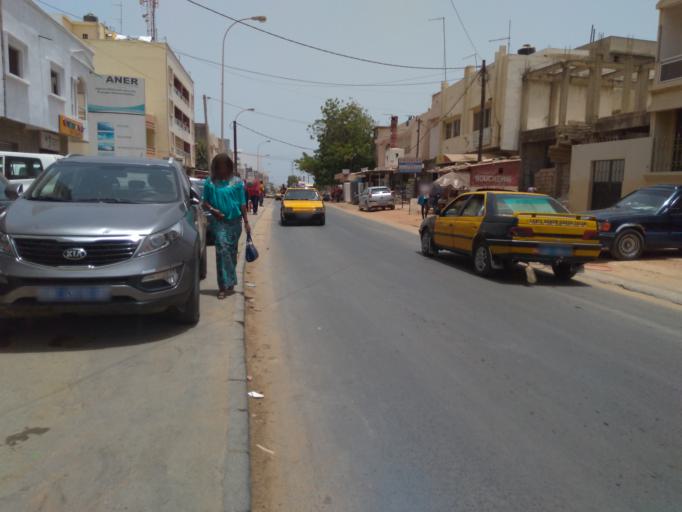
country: SN
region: Dakar
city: Grand Dakar
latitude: 14.7295
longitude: -17.4638
